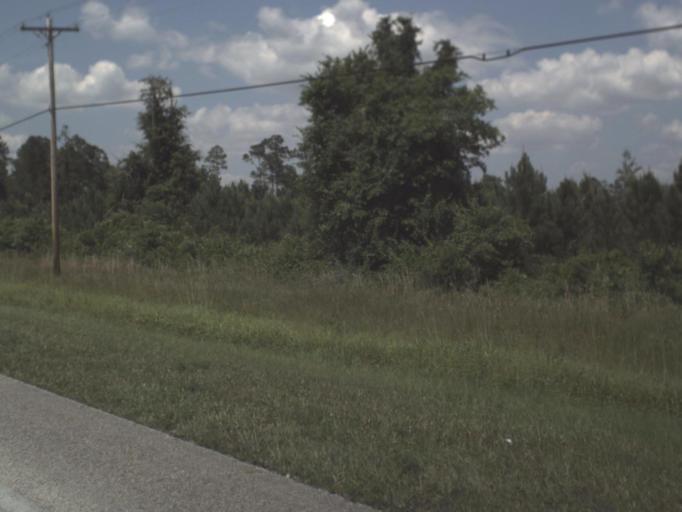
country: US
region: Florida
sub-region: Alachua County
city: Hawthorne
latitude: 29.5707
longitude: -82.0919
